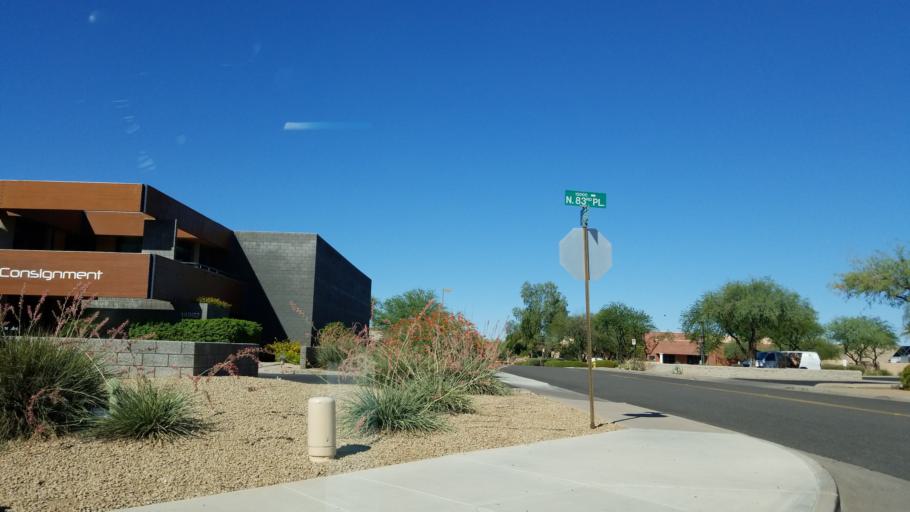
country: US
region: Arizona
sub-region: Maricopa County
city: Paradise Valley
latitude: 33.6225
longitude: -111.8998
